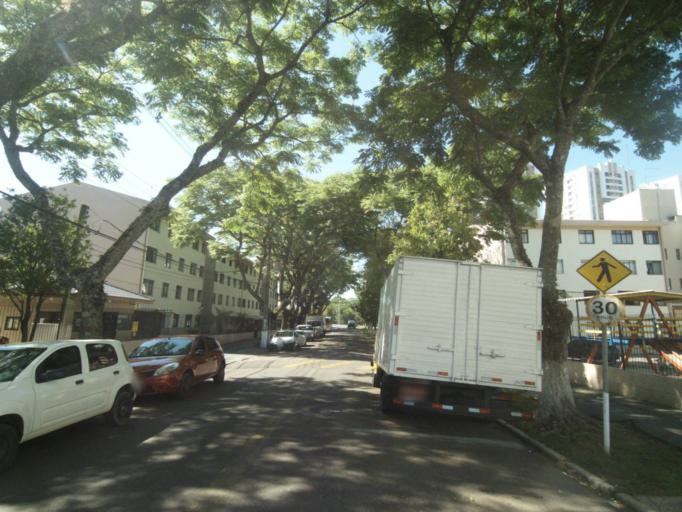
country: BR
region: Parana
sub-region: Curitiba
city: Curitiba
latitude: -25.3861
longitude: -49.2364
